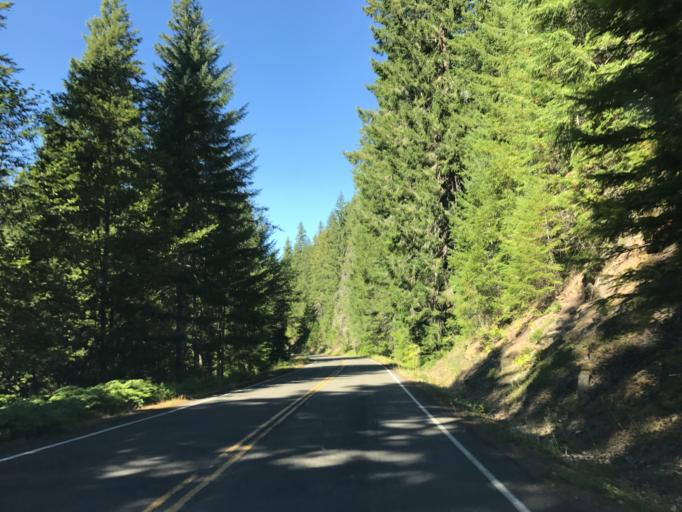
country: US
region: Washington
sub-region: Pierce County
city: Buckley
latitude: 46.7454
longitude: -121.6196
